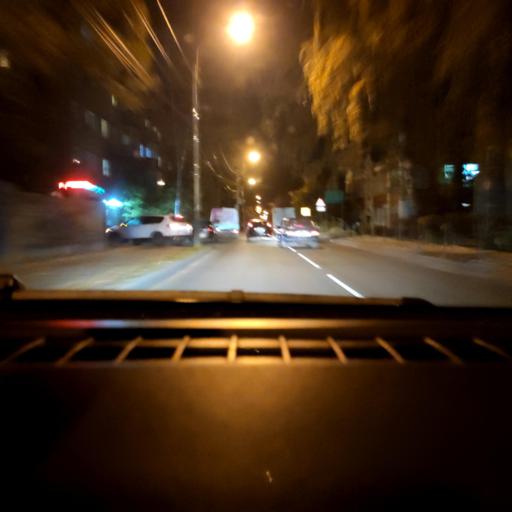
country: RU
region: Voronezj
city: Voronezh
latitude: 51.7158
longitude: 39.2267
